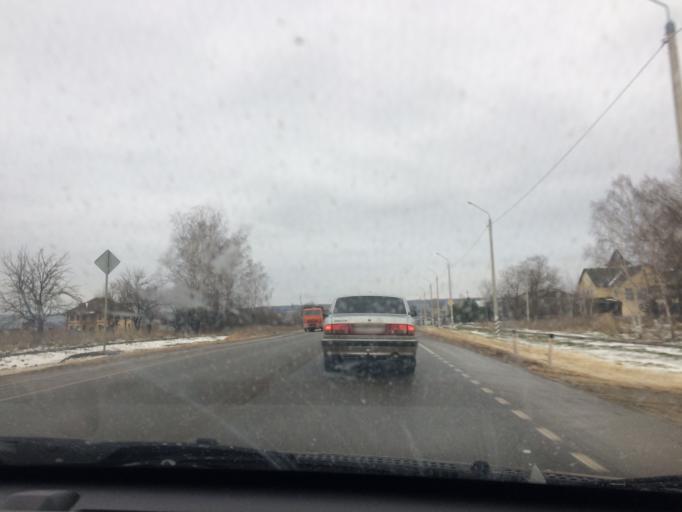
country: RU
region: Tula
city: Gorelki
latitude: 54.2523
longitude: 37.6920
